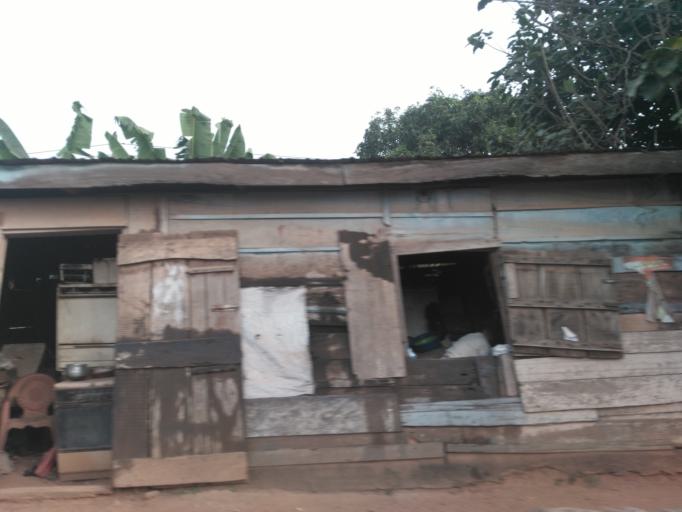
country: GH
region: Ashanti
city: Kumasi
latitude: 6.6941
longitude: -1.6047
